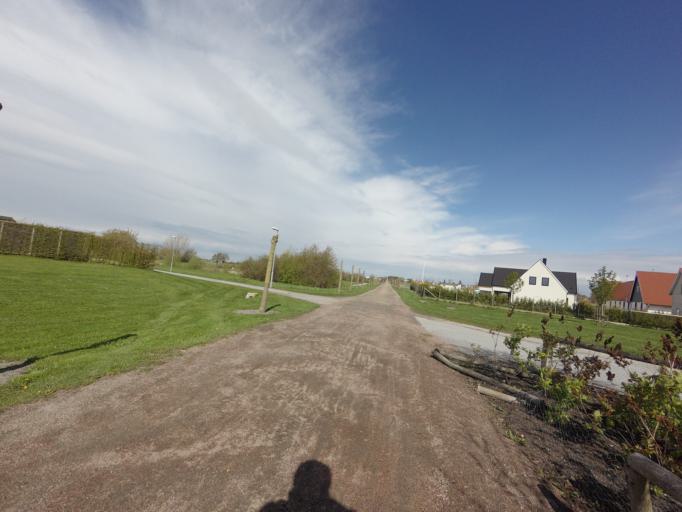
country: SE
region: Skane
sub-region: Malmo
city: Tygelsjo
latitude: 55.5191
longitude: 12.9925
